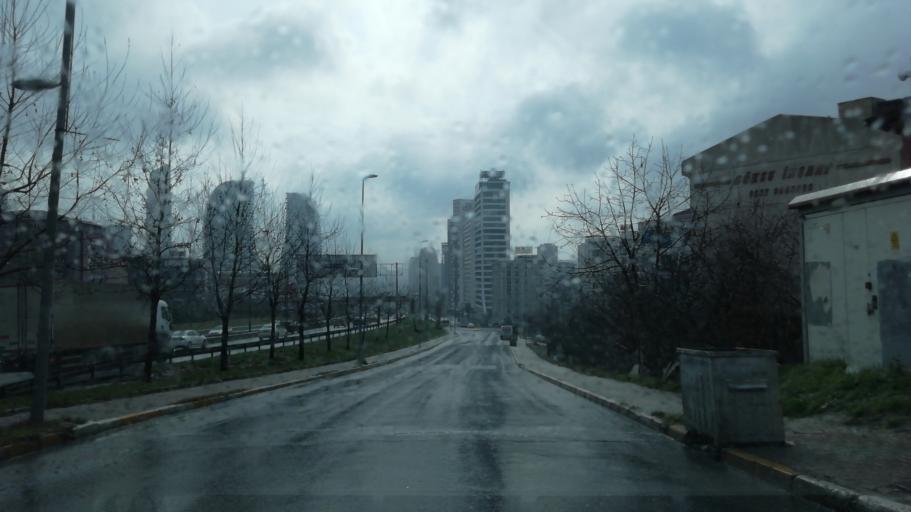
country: TR
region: Istanbul
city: Esenyurt
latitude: 41.0238
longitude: 28.6812
